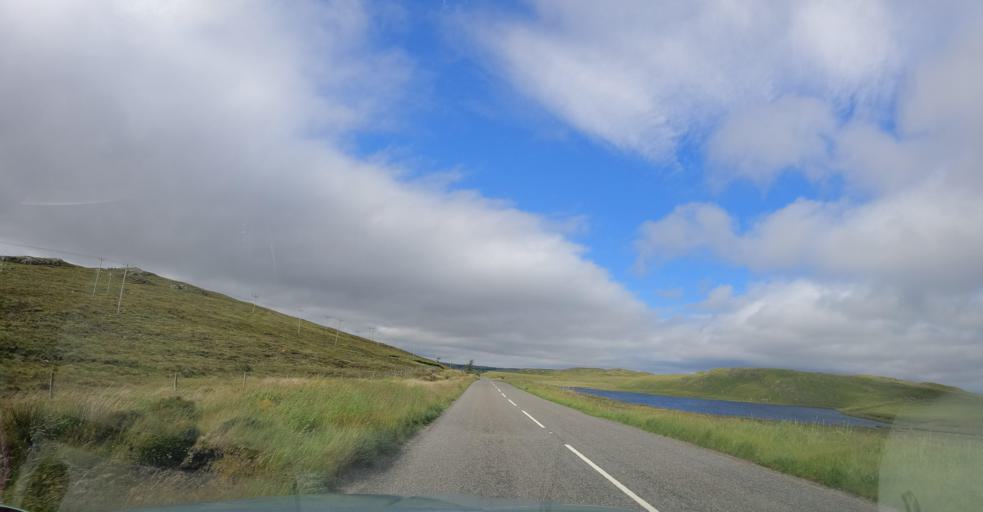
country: GB
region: Scotland
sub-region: Eilean Siar
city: Stornoway
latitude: 58.1270
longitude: -6.5070
